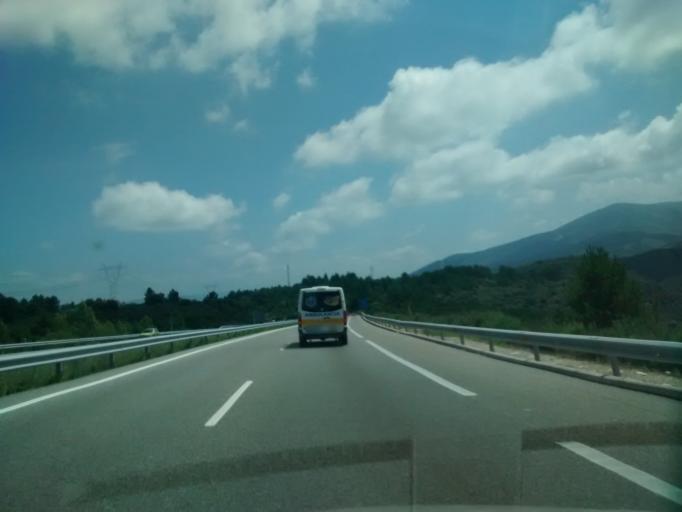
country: ES
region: Castille and Leon
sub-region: Provincia de Leon
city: Molinaseca
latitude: 42.5694
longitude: -6.5436
